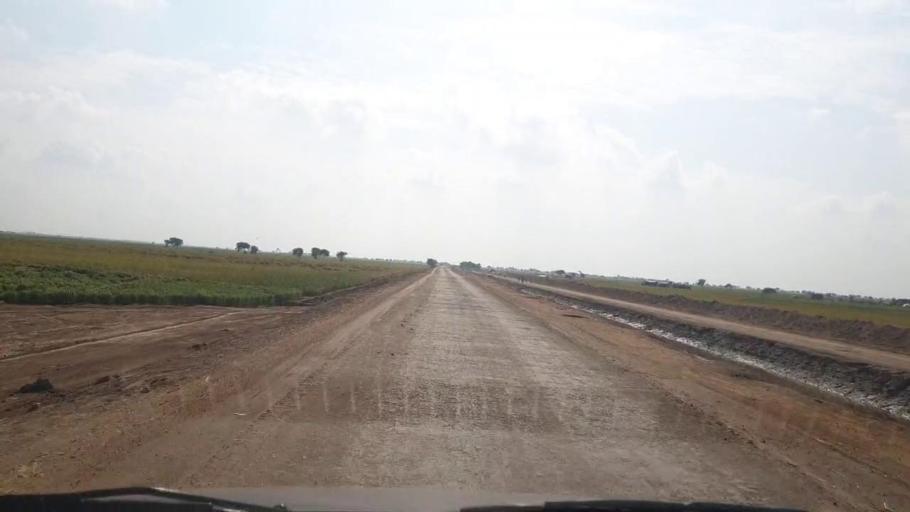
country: PK
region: Sindh
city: Kario
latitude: 24.5822
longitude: 68.5779
